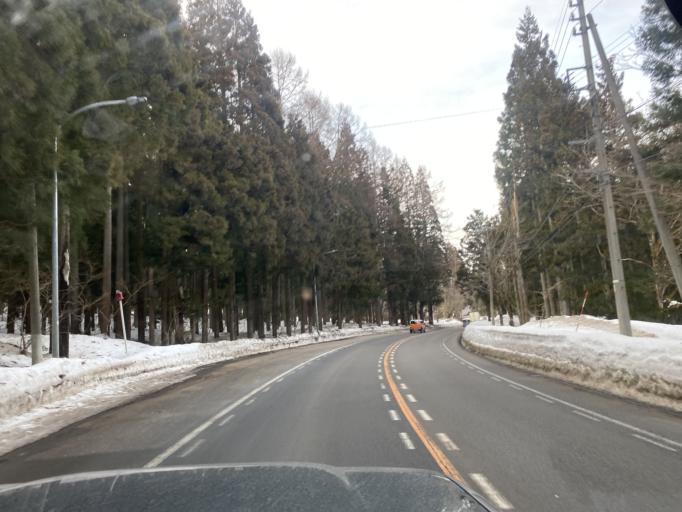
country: JP
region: Nagano
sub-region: Kitaazumi Gun
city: Hakuba
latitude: 36.6274
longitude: 137.8434
